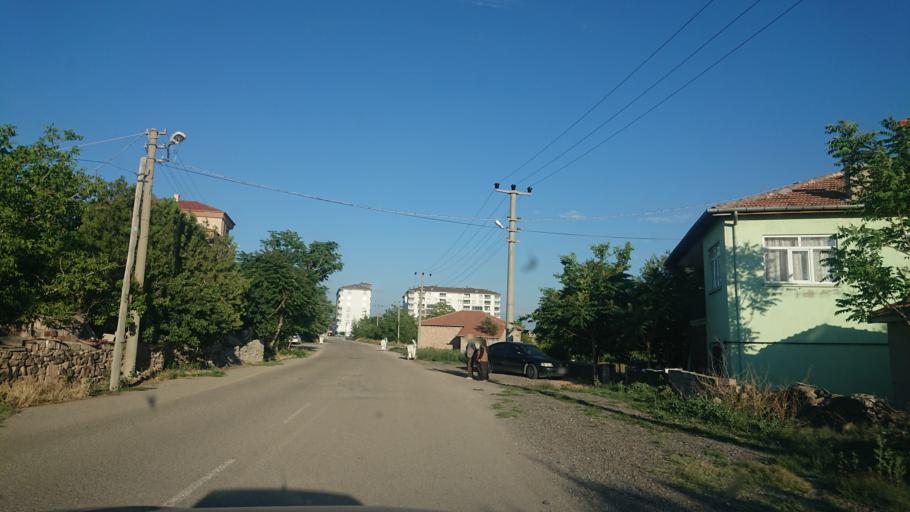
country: TR
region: Aksaray
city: Aksaray
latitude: 38.3894
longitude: 33.9980
